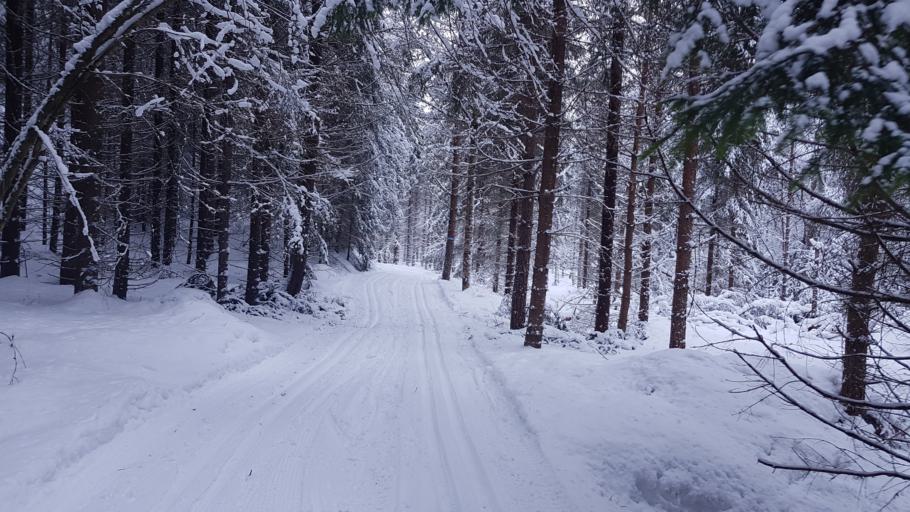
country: NO
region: Akershus
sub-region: Lorenskog
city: Kjenn
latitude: 59.9015
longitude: 10.8769
